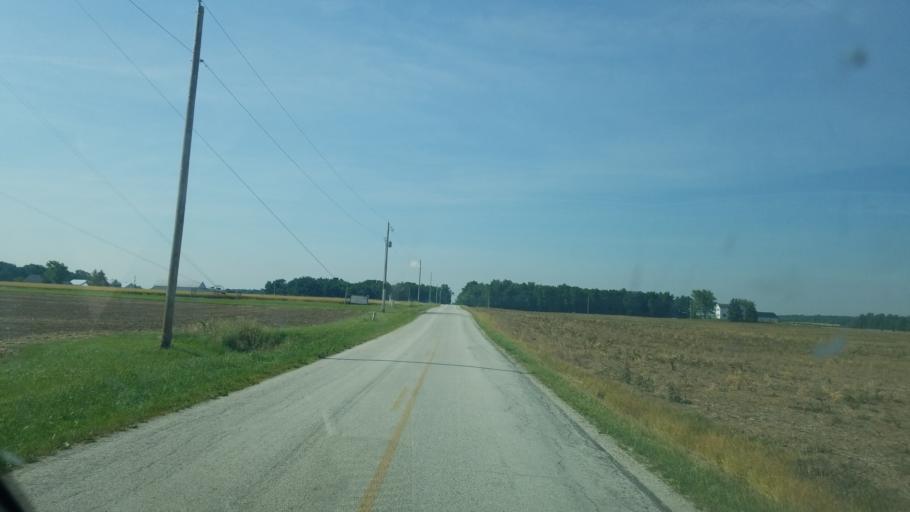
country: US
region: Ohio
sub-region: Wyandot County
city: Carey
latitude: 41.0231
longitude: -83.3629
